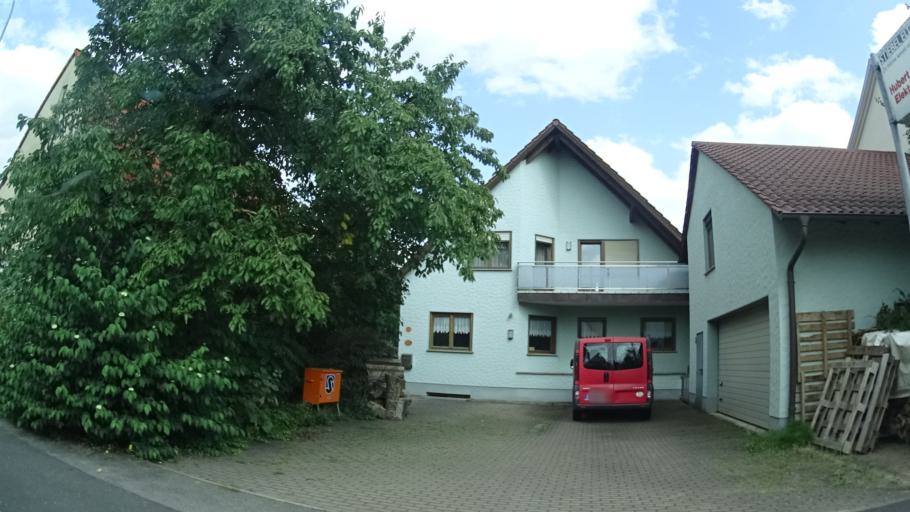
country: DE
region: Bavaria
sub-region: Regierungsbezirk Unterfranken
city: Schwebheim
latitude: 49.9887
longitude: 10.2488
